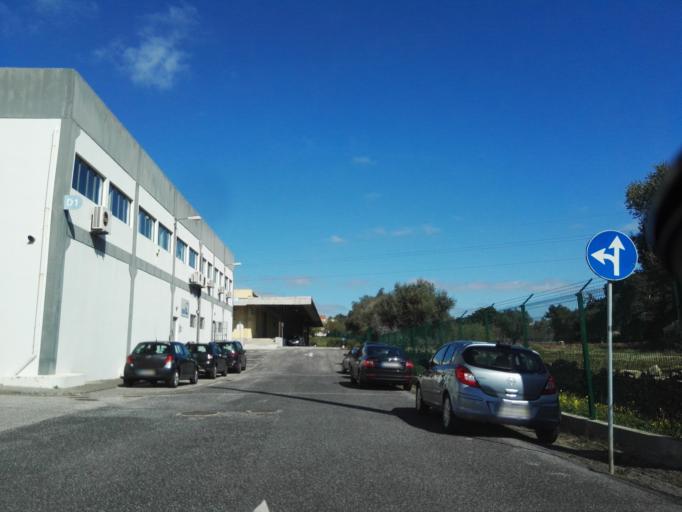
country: PT
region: Lisbon
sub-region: Sintra
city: Rio de Mouro
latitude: 38.7529
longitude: -9.3530
